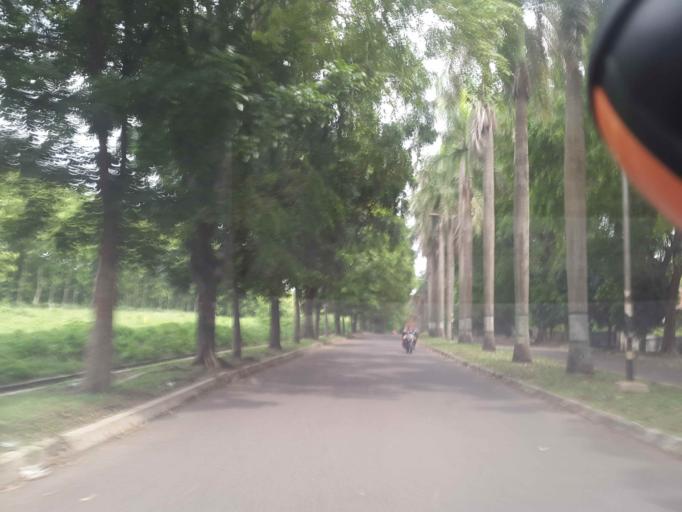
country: ID
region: Banten
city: Curug
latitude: -5.9911
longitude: 106.0428
